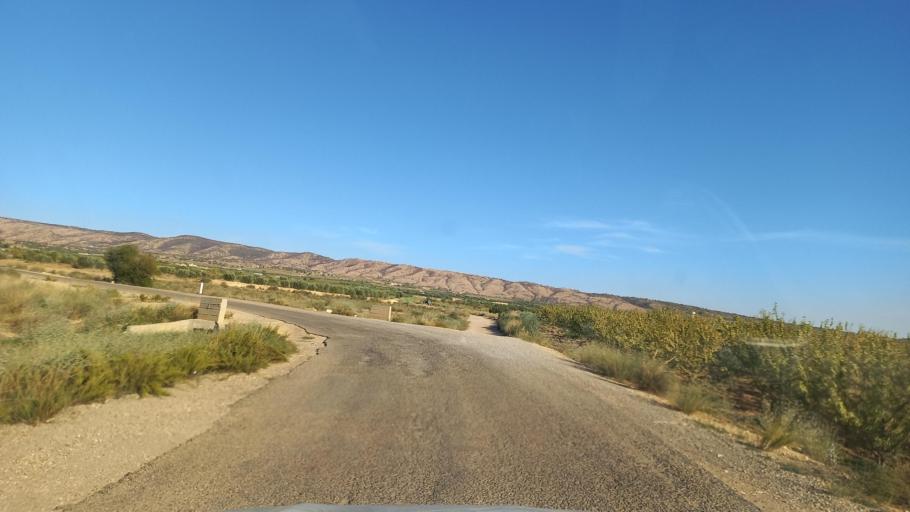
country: TN
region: Al Qasrayn
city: Sbiba
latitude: 35.3342
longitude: 9.1017
